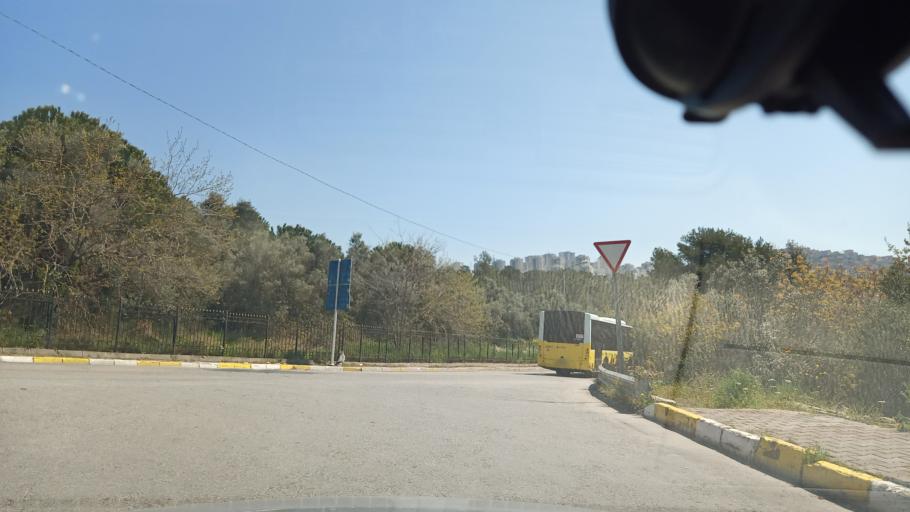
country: TR
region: Istanbul
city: Maltepe
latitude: 40.9480
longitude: 29.1431
